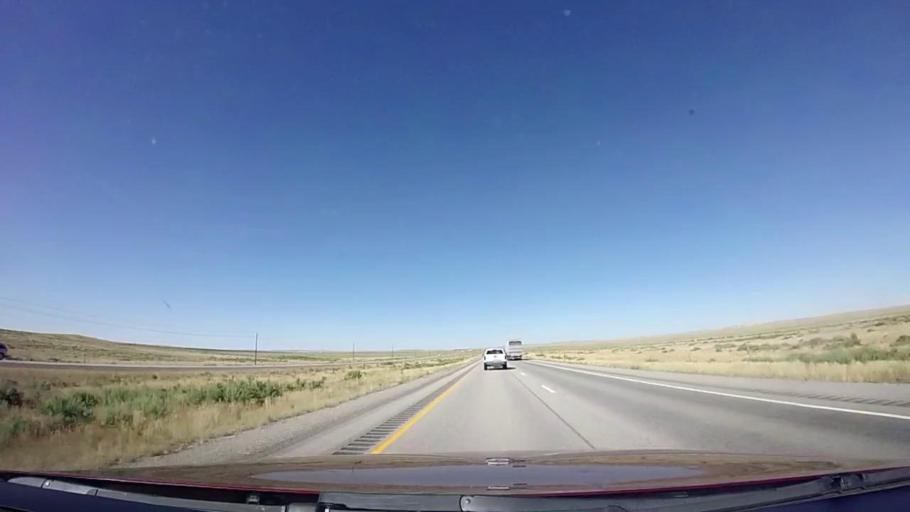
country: US
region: Wyoming
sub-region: Carbon County
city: Rawlins
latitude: 41.7789
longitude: -107.4410
